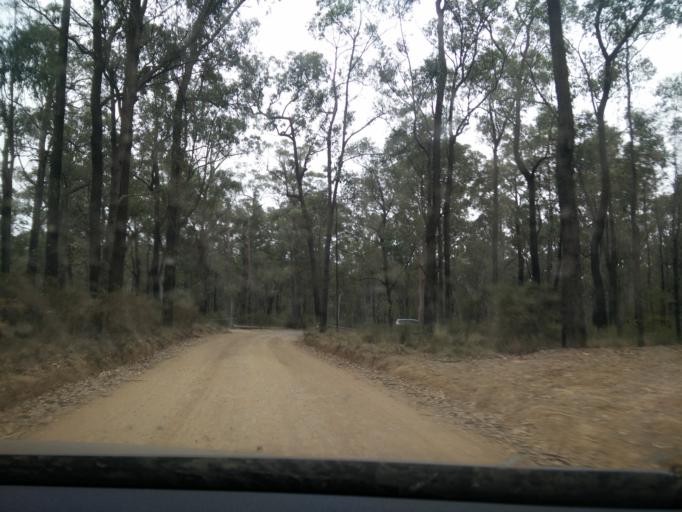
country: AU
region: New South Wales
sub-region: Blue Mountains Municipality
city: Glenbrook
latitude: -33.7920
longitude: 150.6095
